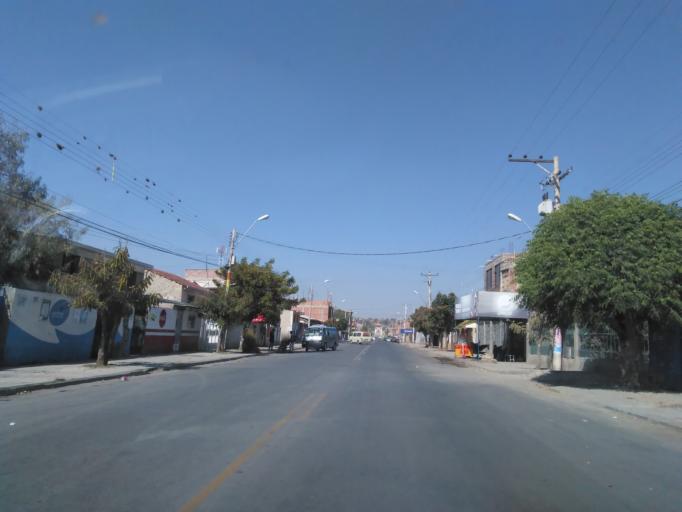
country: BO
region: Cochabamba
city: Sipe Sipe
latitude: -17.4088
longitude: -66.2822
